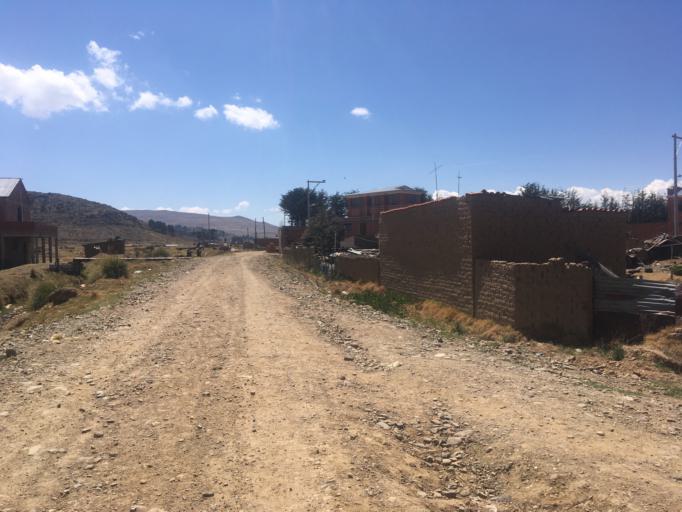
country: BO
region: La Paz
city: Huatajata
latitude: -16.1878
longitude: -68.7444
